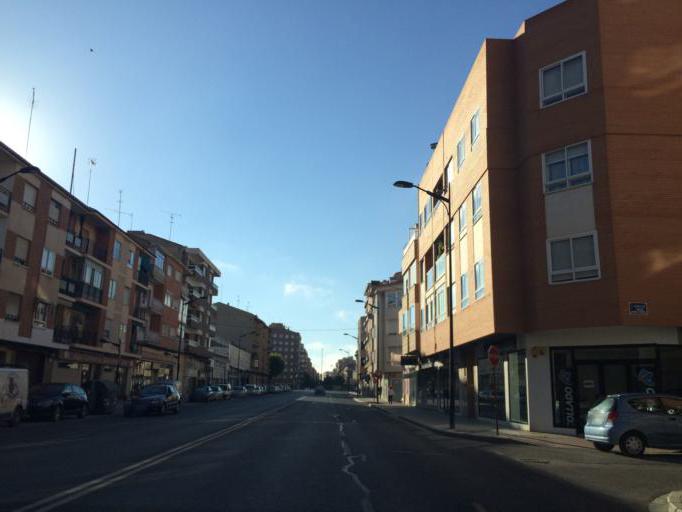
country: ES
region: Castille-La Mancha
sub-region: Provincia de Albacete
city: Albacete
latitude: 39.0054
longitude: -1.8677
